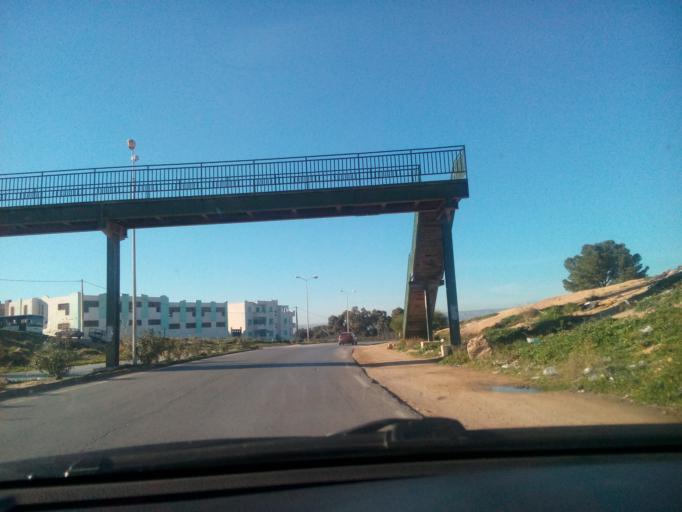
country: DZ
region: Relizane
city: Relizane
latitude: 35.7092
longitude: 0.5100
